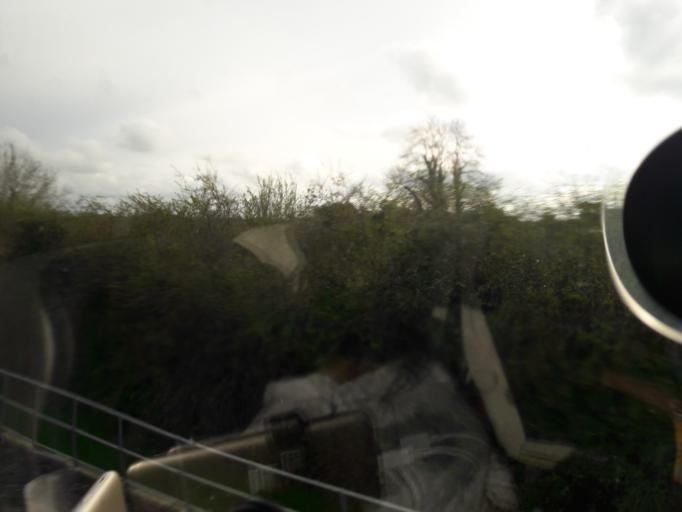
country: IE
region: Leinster
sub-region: An Mhi
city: Longwood
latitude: 53.4492
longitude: -6.9534
